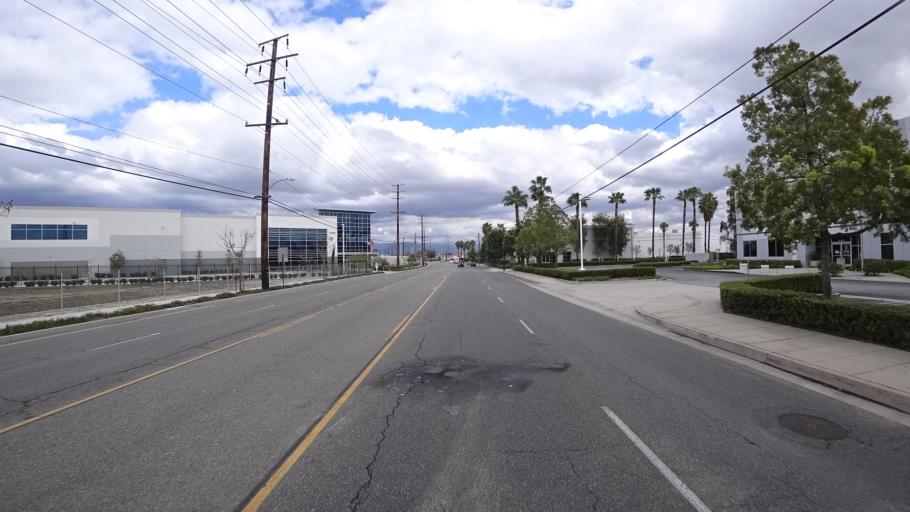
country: US
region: California
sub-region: Los Angeles County
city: North El Monte
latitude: 34.0884
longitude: -118.0010
